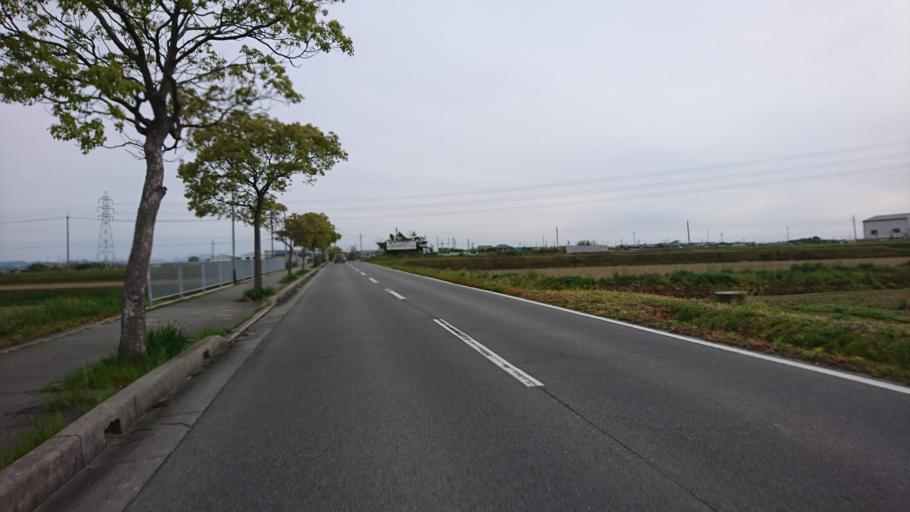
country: JP
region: Hyogo
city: Kakogawacho-honmachi
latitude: 34.7562
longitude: 134.9071
